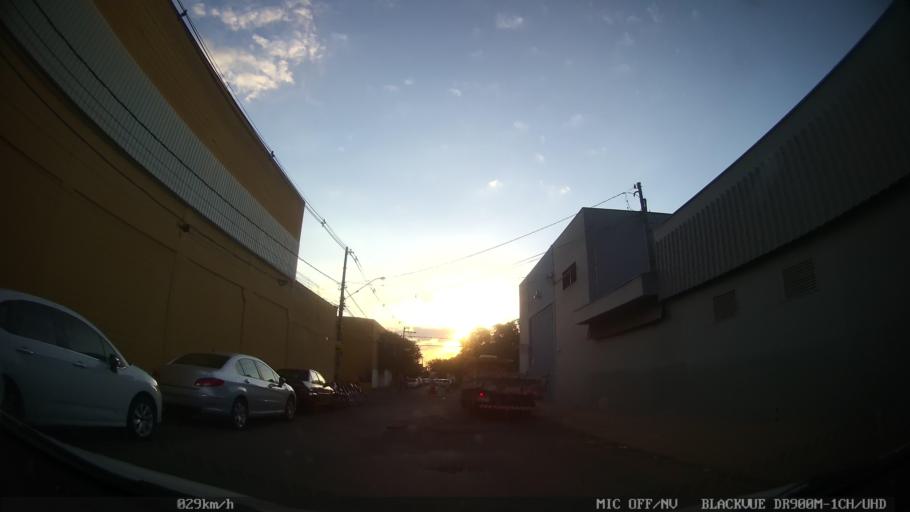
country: BR
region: Sao Paulo
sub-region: Ribeirao Preto
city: Ribeirao Preto
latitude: -21.1457
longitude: -47.7900
